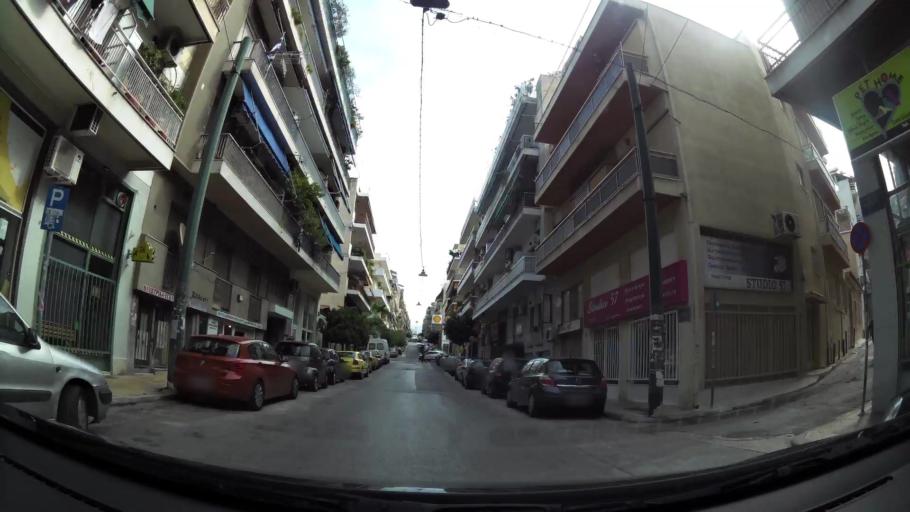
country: GR
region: Attica
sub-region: Nomarchia Athinas
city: Athens
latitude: 37.9753
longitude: 23.7144
